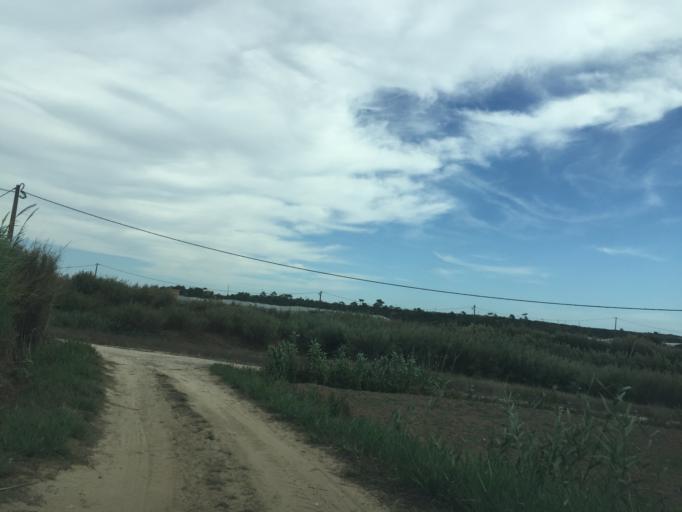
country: PT
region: Lisbon
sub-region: Lourinha
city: Lourinha
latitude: 39.1880
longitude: -9.3430
